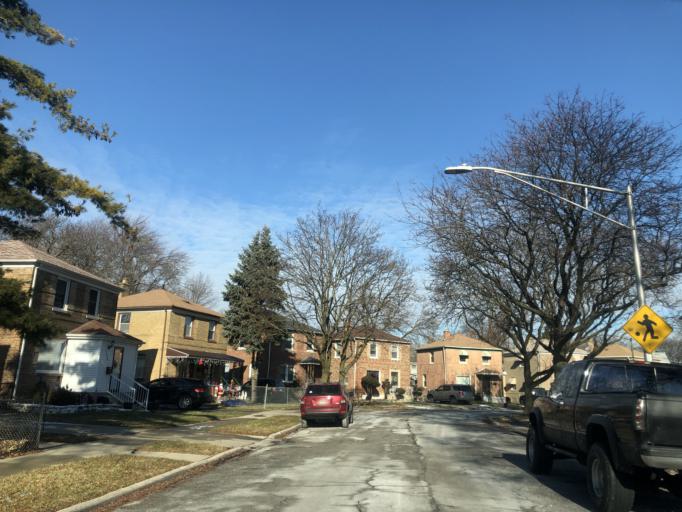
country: US
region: Illinois
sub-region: Cook County
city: Evergreen Park
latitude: 41.7557
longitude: -87.6763
